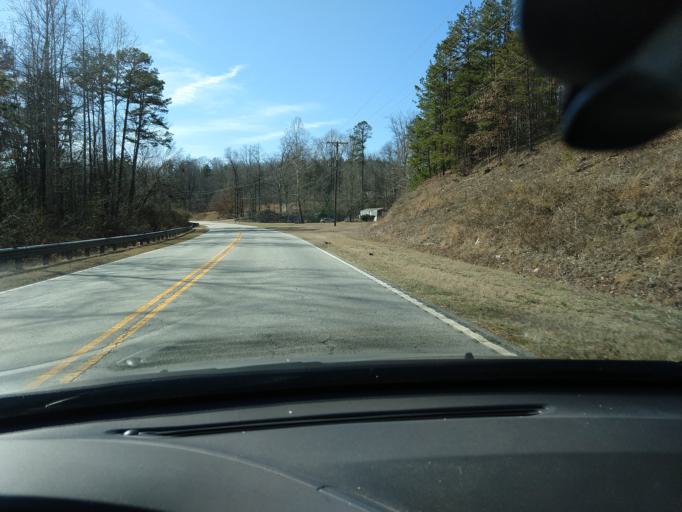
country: US
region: South Carolina
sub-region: Oconee County
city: Westminster
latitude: 34.6179
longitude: -83.1418
